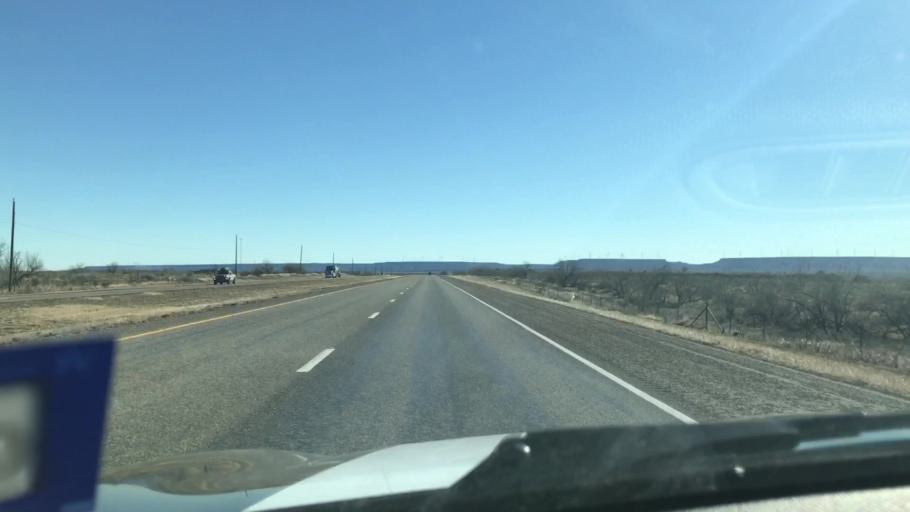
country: US
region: Texas
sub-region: Garza County
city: Post
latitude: 33.0866
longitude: -101.2429
